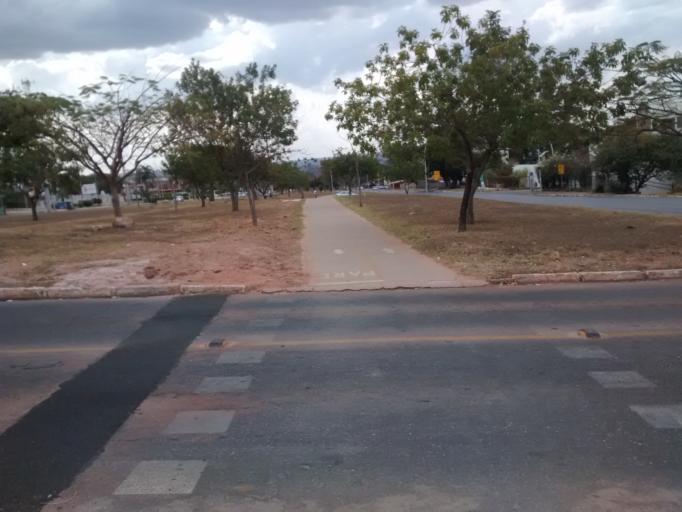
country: BR
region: Federal District
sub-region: Brasilia
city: Brasilia
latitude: -15.7485
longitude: -47.8991
